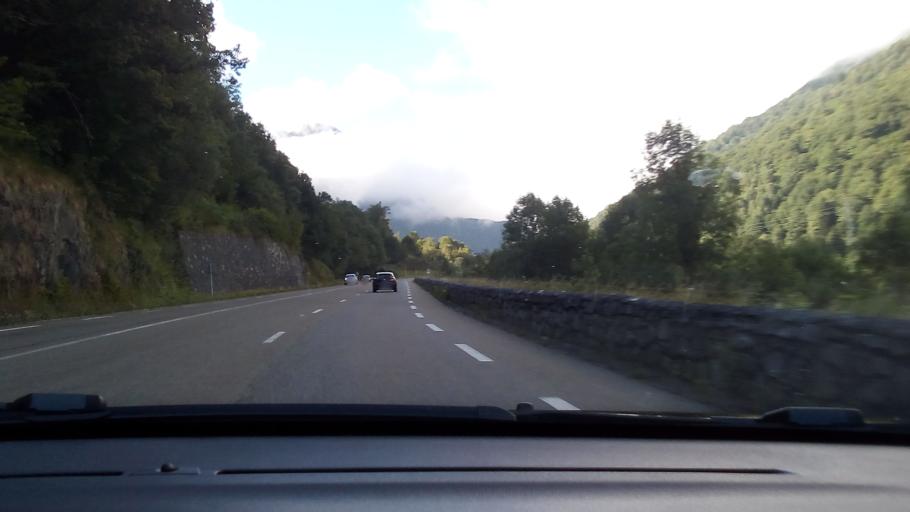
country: ES
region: Aragon
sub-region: Provincia de Huesca
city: Canfranc
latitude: 42.8661
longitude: -0.5497
